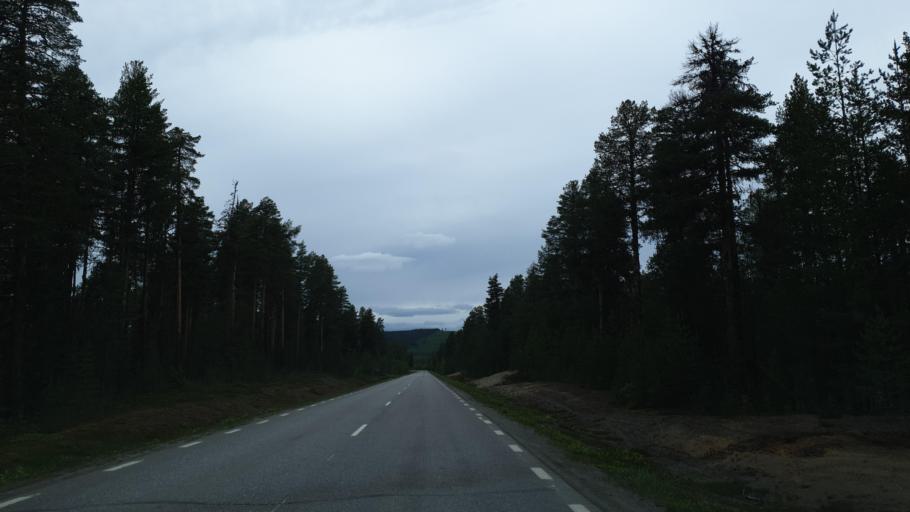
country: SE
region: Vaesterbotten
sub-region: Sorsele Kommun
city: Sorsele
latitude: 65.5496
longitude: 17.5078
